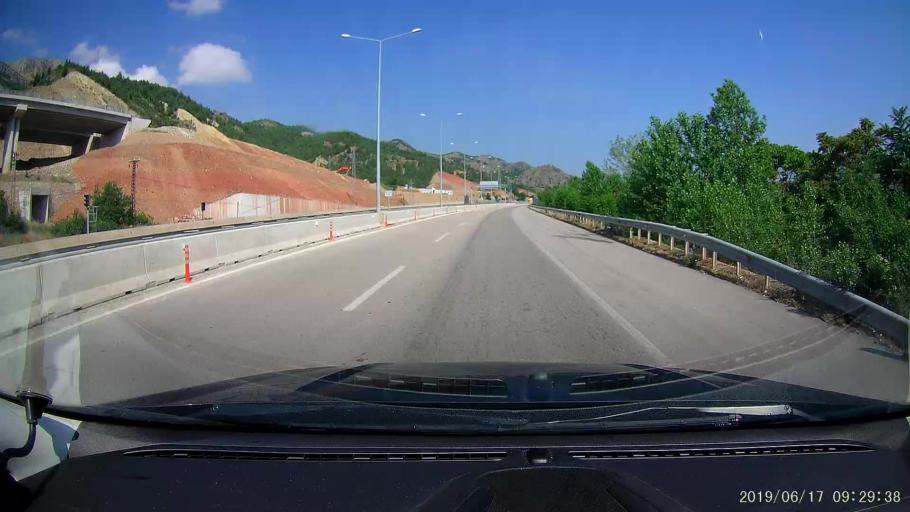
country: TR
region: Amasya
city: Amasya
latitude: 40.6981
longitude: 35.8095
